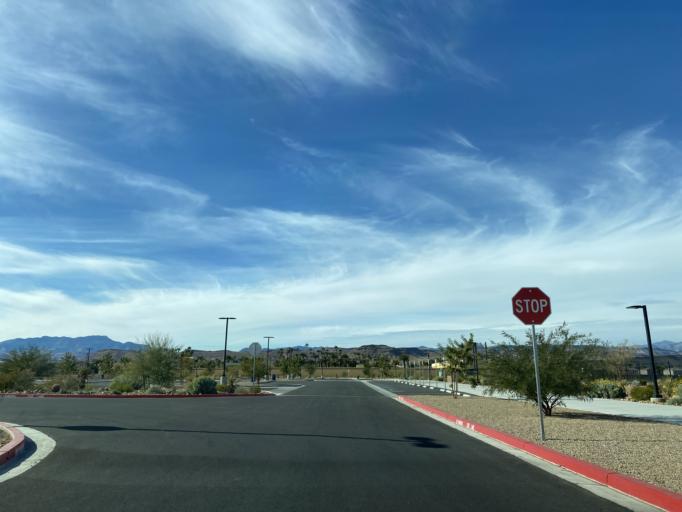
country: US
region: Nevada
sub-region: Clark County
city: Enterprise
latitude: 36.0491
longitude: -115.2757
